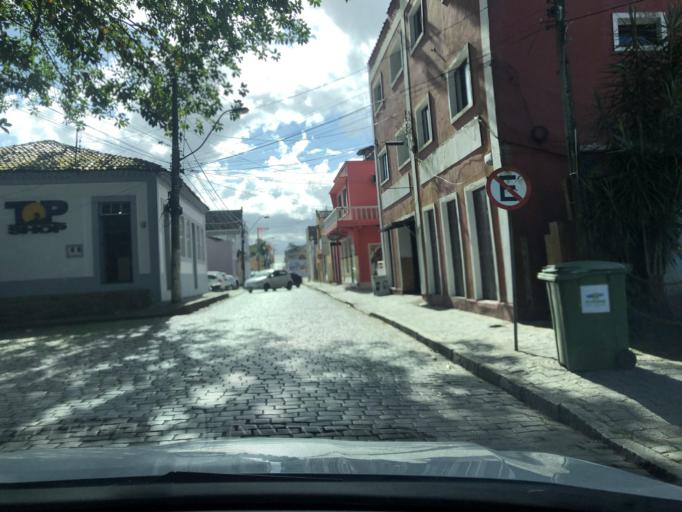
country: BR
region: Santa Catarina
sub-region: Sao Francisco Do Sul
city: Sao Francisco do Sul
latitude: -26.2420
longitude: -48.6360
